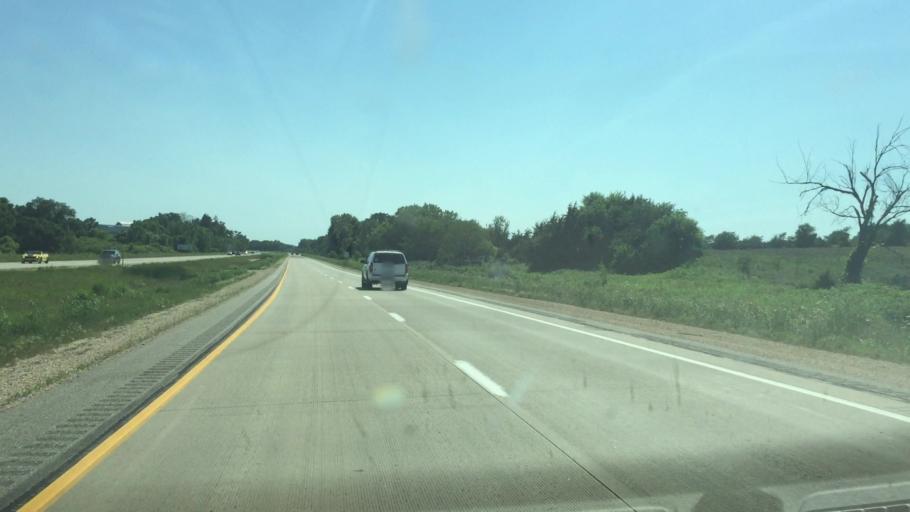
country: US
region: Iowa
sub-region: Jones County
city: Monticello
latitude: 42.2050
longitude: -91.2016
